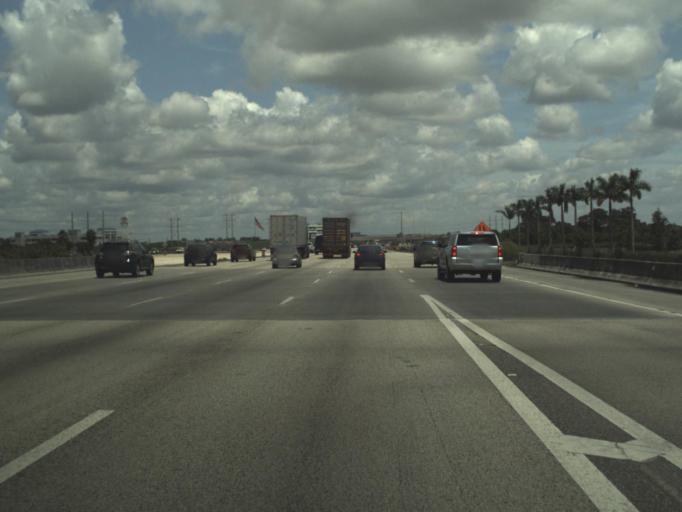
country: US
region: Florida
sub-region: Broward County
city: Southwest Ranches
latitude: 26.0687
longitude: -80.3561
